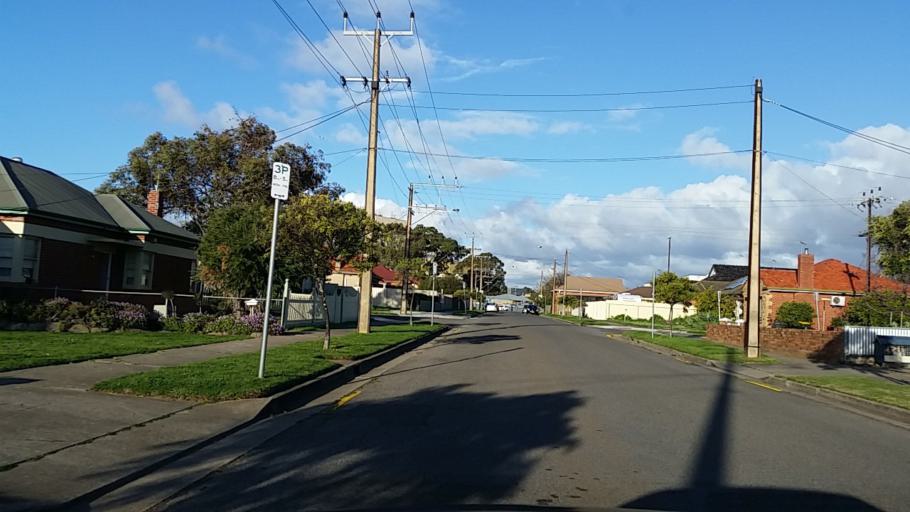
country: AU
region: South Australia
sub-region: Charles Sturt
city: Woodville West
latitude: -34.8847
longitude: 138.5291
